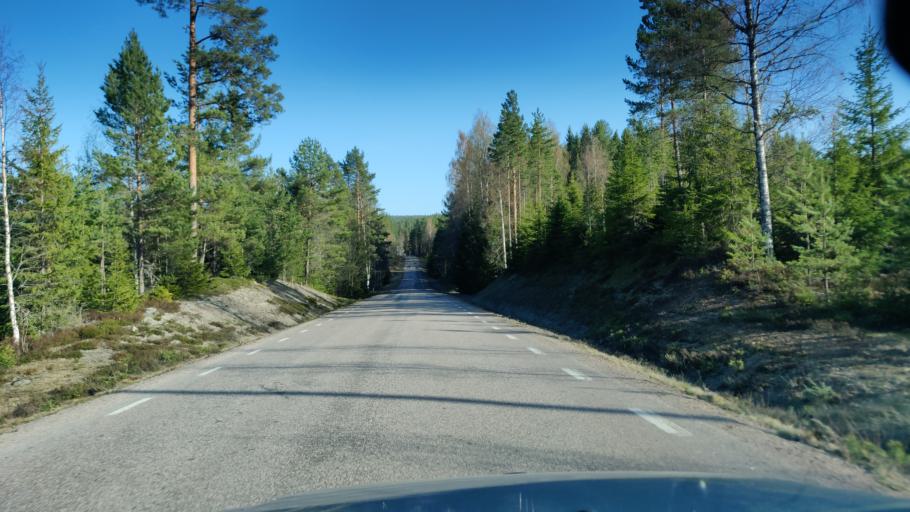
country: SE
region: Vaermland
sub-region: Sunne Kommun
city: Sunne
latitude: 59.9899
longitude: 13.3106
